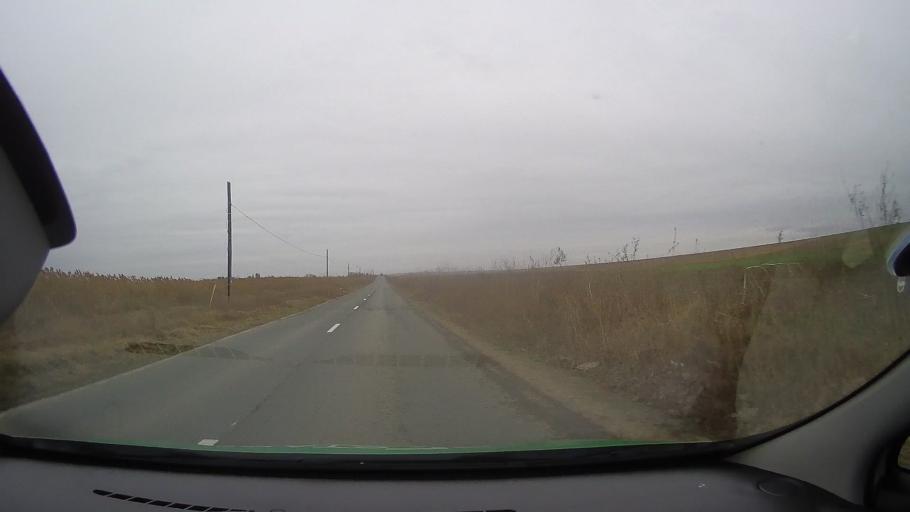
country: RO
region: Constanta
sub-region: Comuna Silistea
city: Silistea
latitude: 44.4359
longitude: 28.2228
